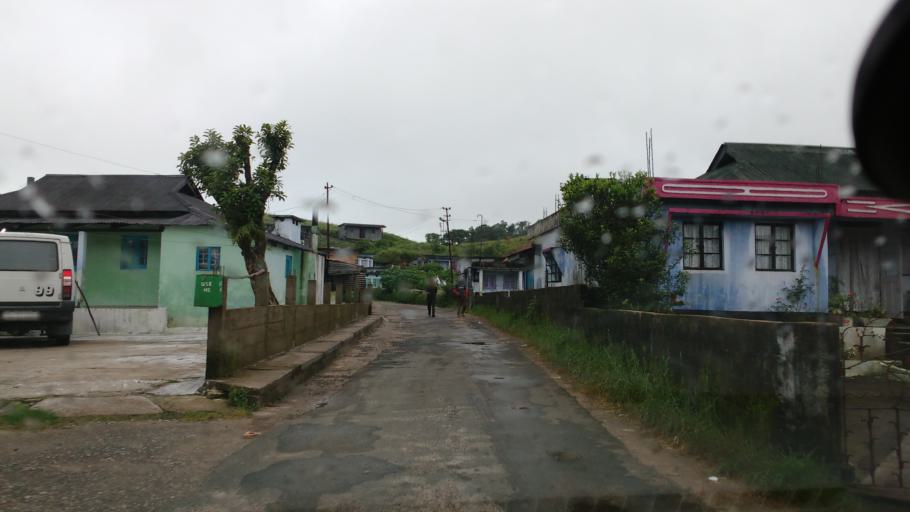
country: IN
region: Meghalaya
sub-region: East Khasi Hills
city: Cherrapunji
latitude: 25.2435
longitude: 91.7313
